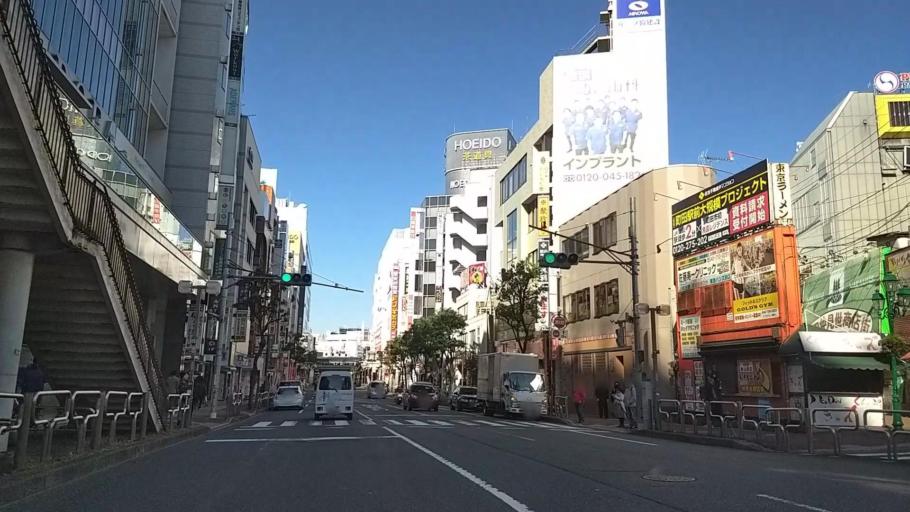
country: JP
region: Tokyo
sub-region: Machida-shi
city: Machida
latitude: 35.5411
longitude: 139.4484
